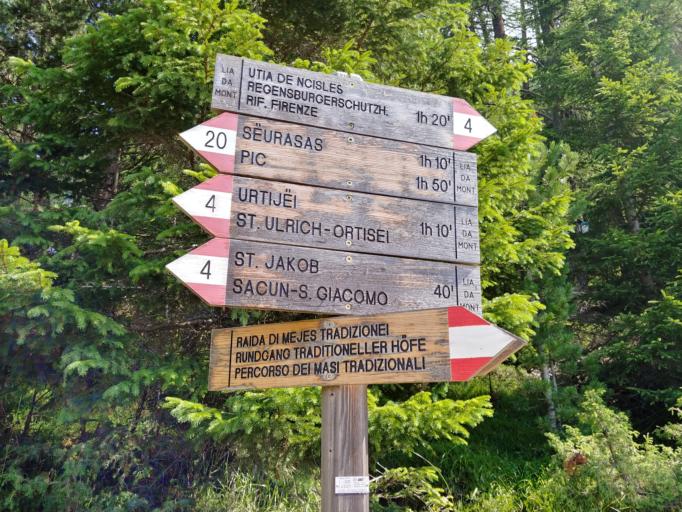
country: IT
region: Trentino-Alto Adige
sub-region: Bolzano
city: Santa Cristina Valgardena
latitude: 46.5683
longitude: 11.7218
